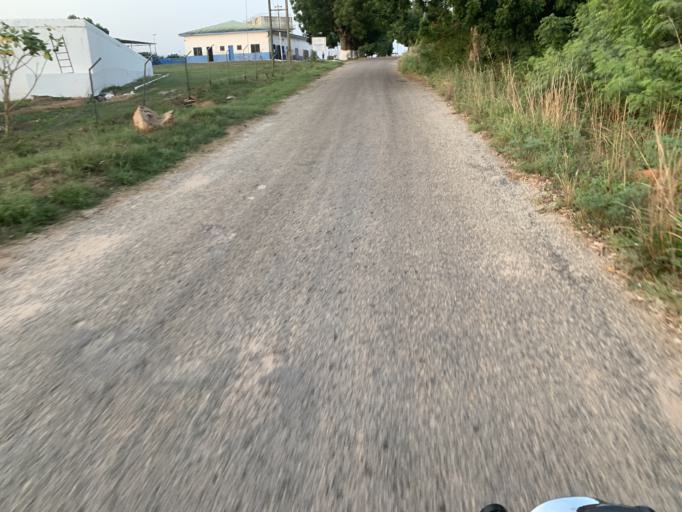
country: GH
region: Central
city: Winneba
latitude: 5.3667
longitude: -0.6193
